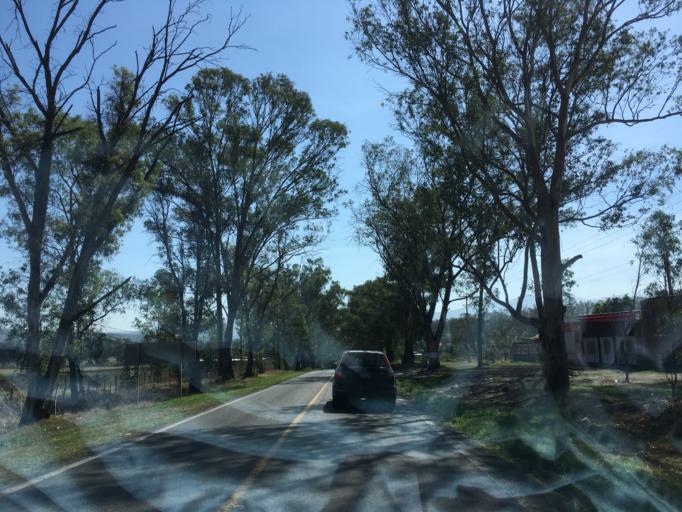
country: MX
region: Michoacan
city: Charo
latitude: 19.6822
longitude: -101.0550
